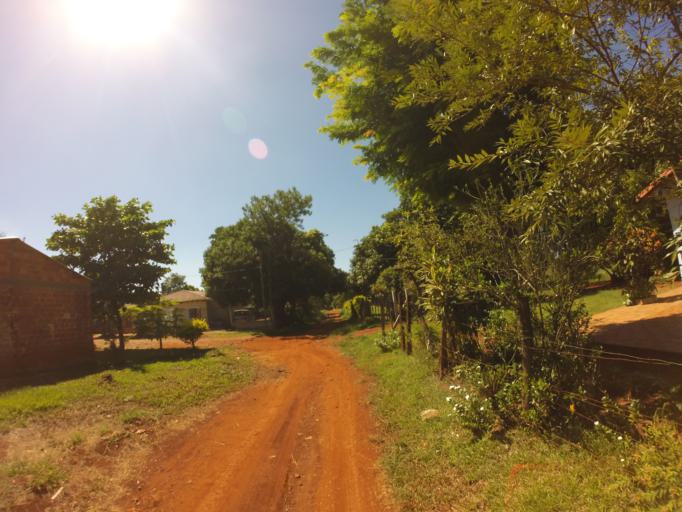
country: PY
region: Alto Parana
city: Ciudad del Este
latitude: -25.4360
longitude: -54.6459
